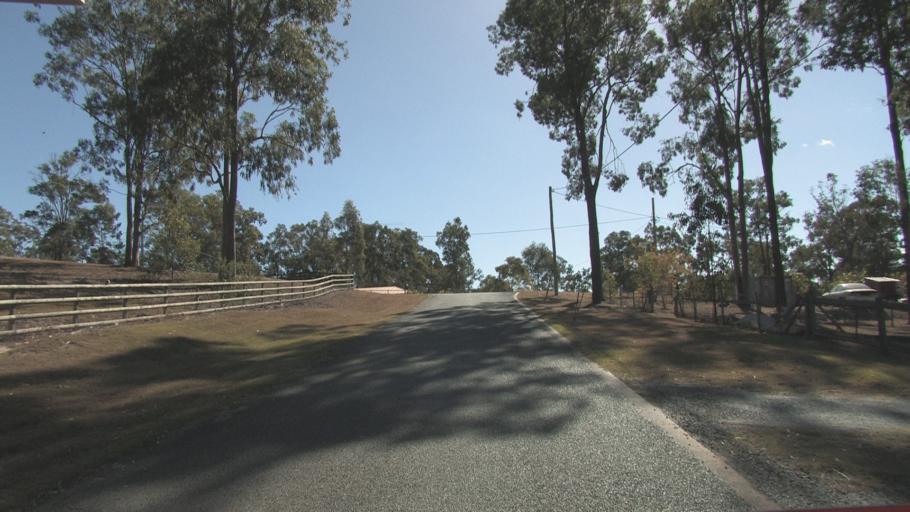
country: AU
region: Queensland
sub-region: Logan
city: Cedar Vale
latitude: -27.8830
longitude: 153.0036
